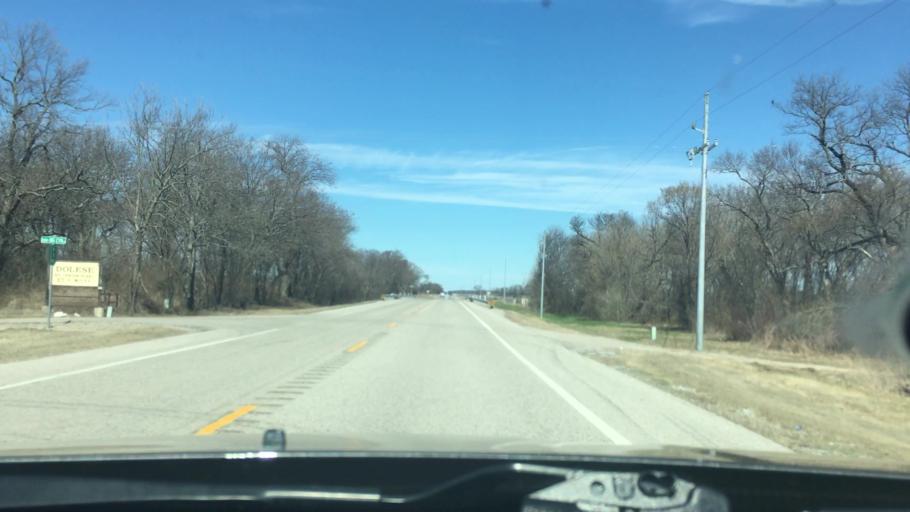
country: US
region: Oklahoma
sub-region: Murray County
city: Sulphur
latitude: 34.3613
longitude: -96.9508
